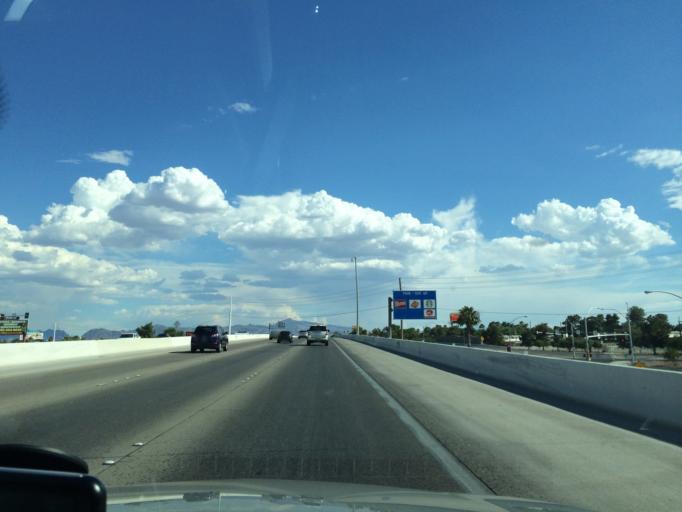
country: US
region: Nevada
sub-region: Clark County
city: Winchester
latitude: 36.1383
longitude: -115.0909
